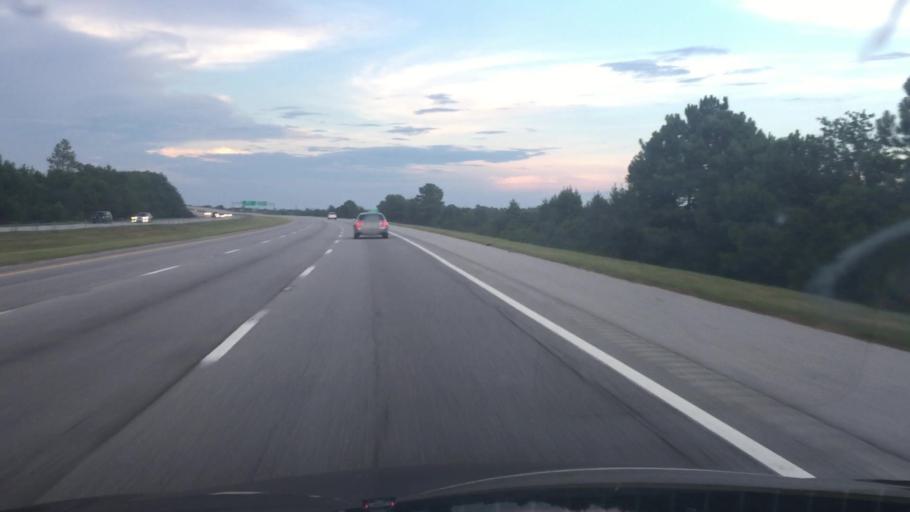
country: US
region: South Carolina
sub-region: Horry County
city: North Myrtle Beach
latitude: 33.8363
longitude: -78.7089
